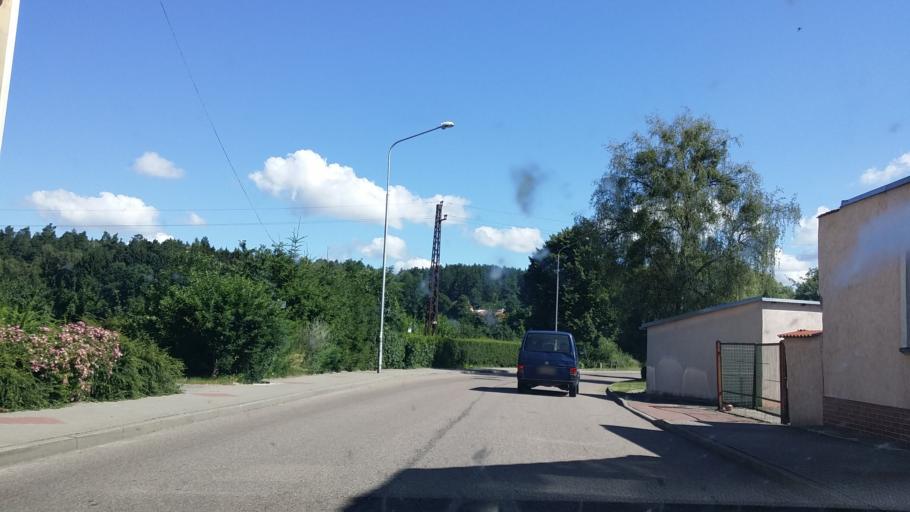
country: PL
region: West Pomeranian Voivodeship
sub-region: Powiat drawski
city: Kalisz Pomorski
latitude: 53.2993
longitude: 15.9065
